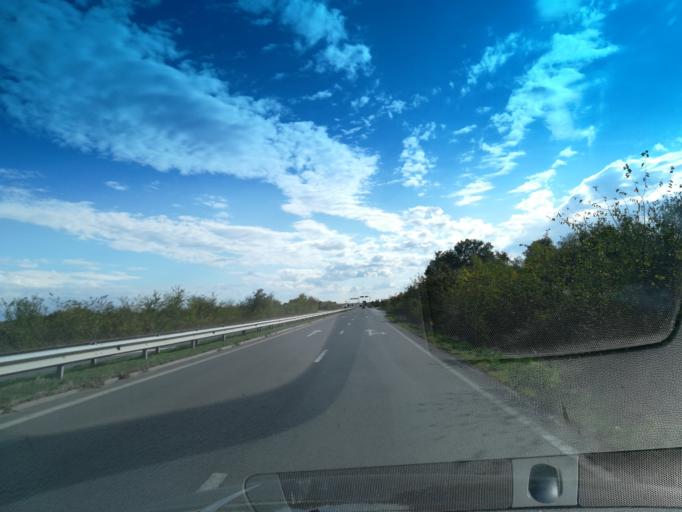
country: BG
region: Stara Zagora
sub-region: Obshtina Stara Zagora
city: Stara Zagora
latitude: 42.3450
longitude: 25.6604
